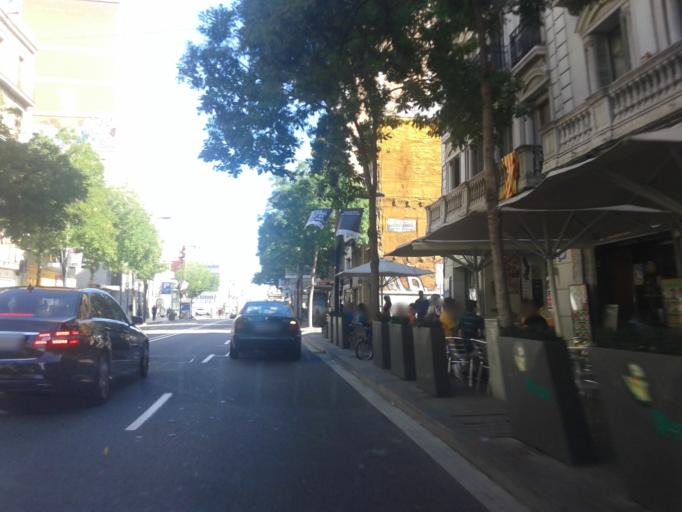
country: ES
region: Catalonia
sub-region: Provincia de Barcelona
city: Sants-Montjuic
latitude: 41.3752
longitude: 2.1468
